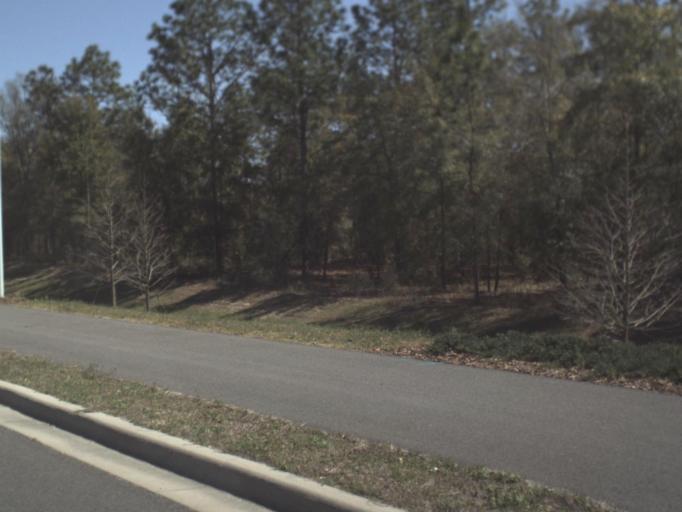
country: US
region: Florida
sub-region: Leon County
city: Tallahassee
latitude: 30.3756
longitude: -84.2742
